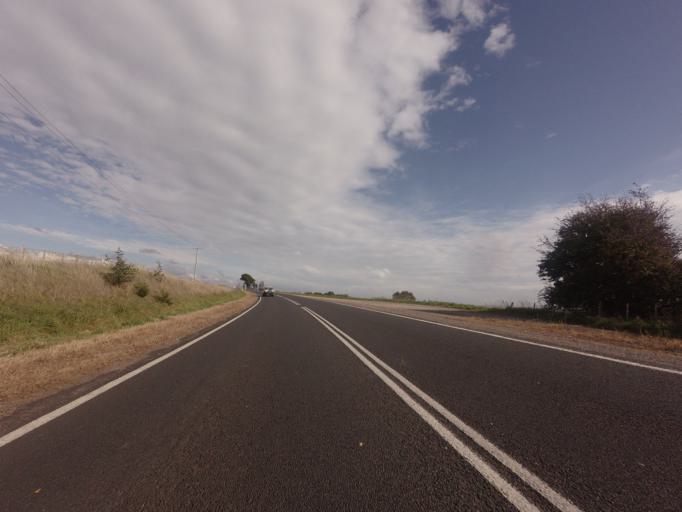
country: AU
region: Tasmania
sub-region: Meander Valley
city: Deloraine
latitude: -41.5186
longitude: 146.7226
